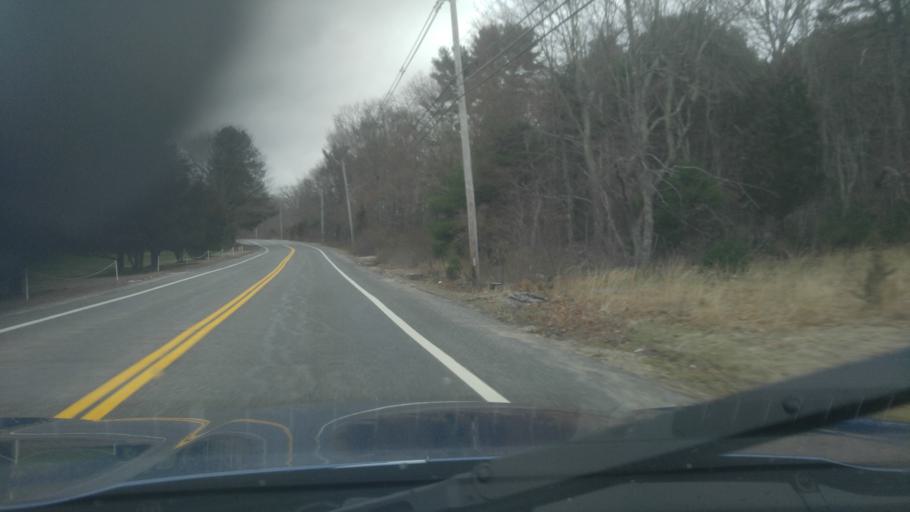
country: US
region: Rhode Island
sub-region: Kent County
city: West Greenwich
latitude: 41.6718
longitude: -71.6319
